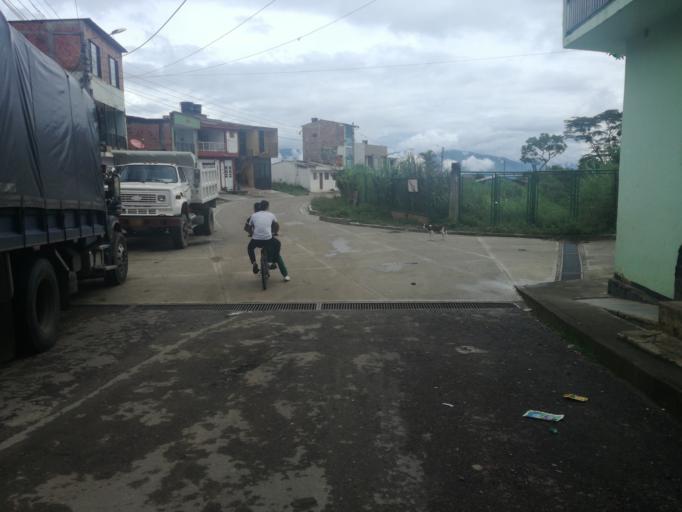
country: CO
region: Boyaca
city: Santana
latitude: 6.0587
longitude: -73.4836
